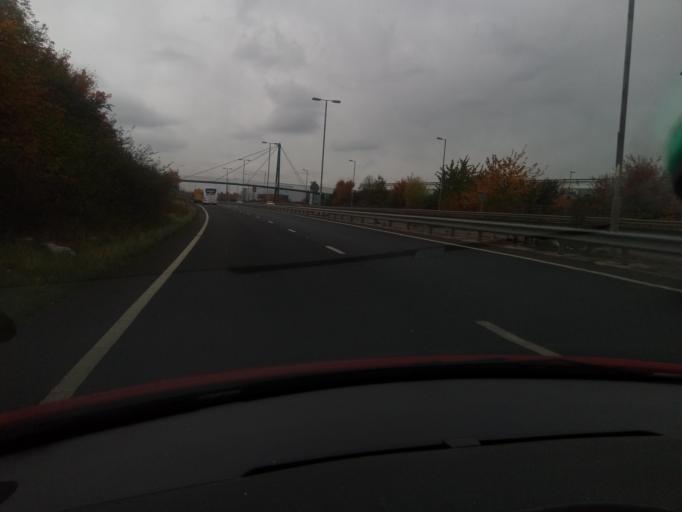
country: GB
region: England
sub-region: Derbyshire
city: Borrowash
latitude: 52.8992
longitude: -1.4178
